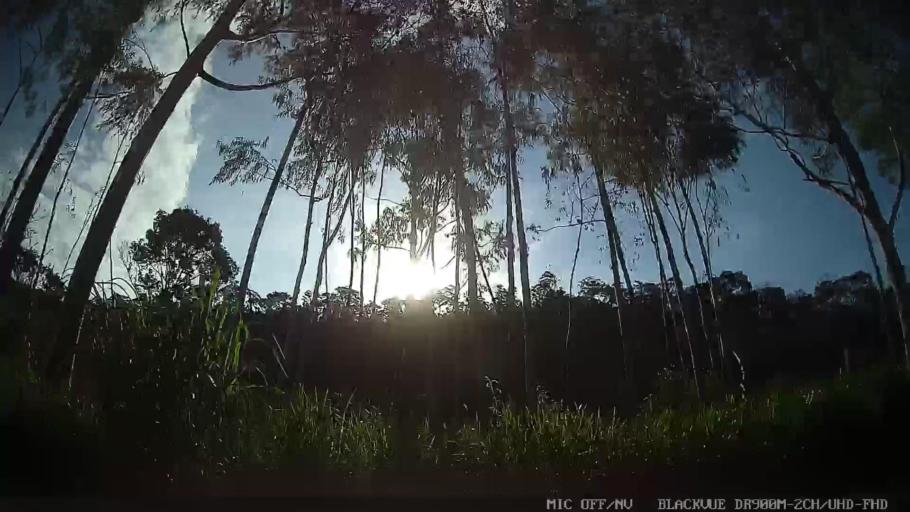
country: BR
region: Sao Paulo
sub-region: Serra Negra
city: Serra Negra
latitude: -22.6702
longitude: -46.6850
